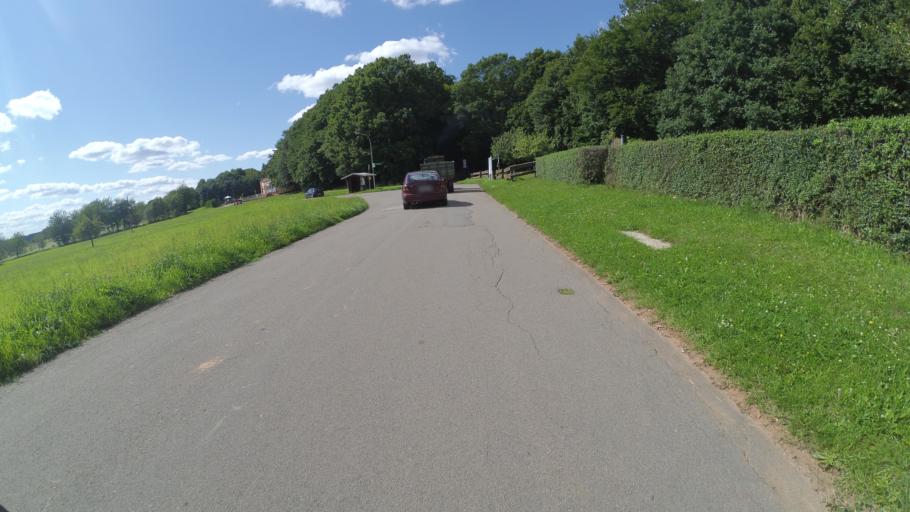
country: DE
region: Saarland
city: Mainzweiler
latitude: 49.4370
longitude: 7.0960
